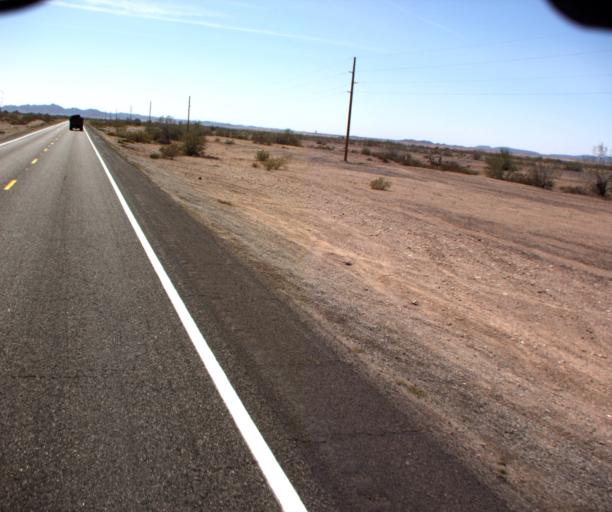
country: US
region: Arizona
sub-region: Yuma County
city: Fortuna Foothills
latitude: 32.9104
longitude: -114.3268
